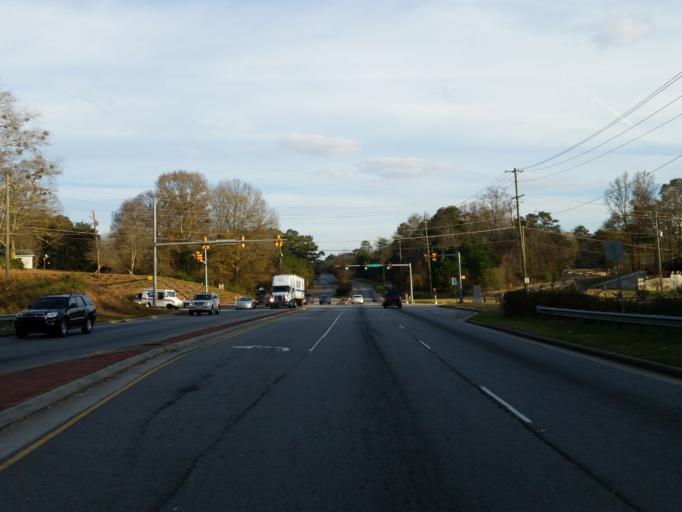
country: US
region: Georgia
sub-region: Cobb County
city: Powder Springs
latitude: 33.8667
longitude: -84.6863
